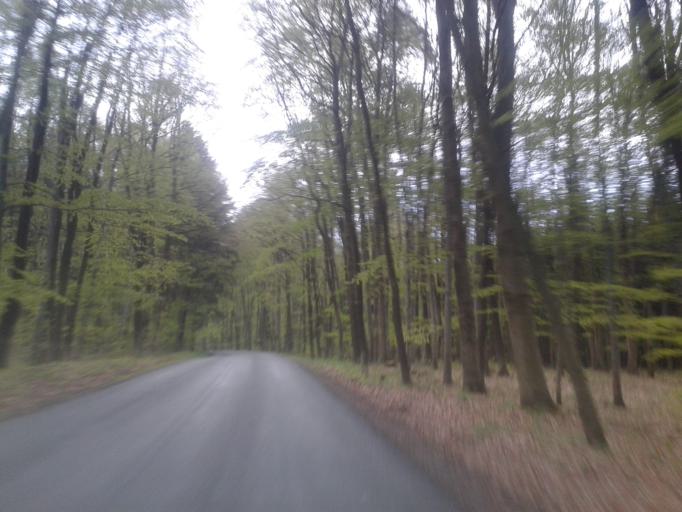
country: CZ
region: Central Bohemia
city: Hudlice
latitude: 49.9420
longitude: 13.9138
